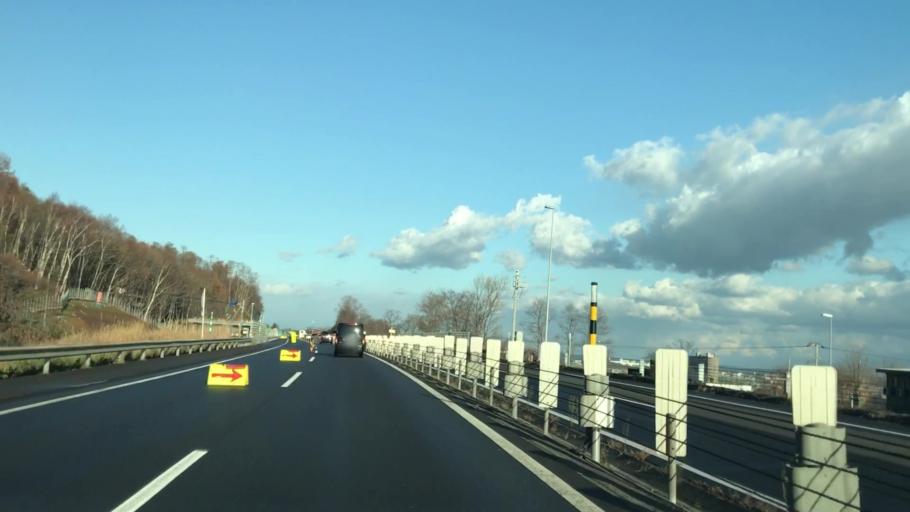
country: JP
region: Hokkaido
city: Sapporo
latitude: 43.1100
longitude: 141.2402
